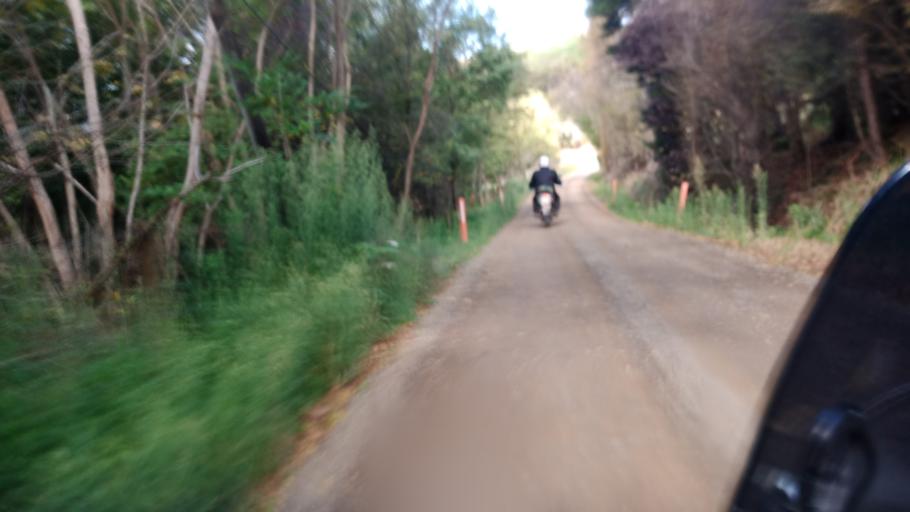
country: NZ
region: Gisborne
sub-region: Gisborne District
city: Gisborne
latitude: -38.4602
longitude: 177.6438
